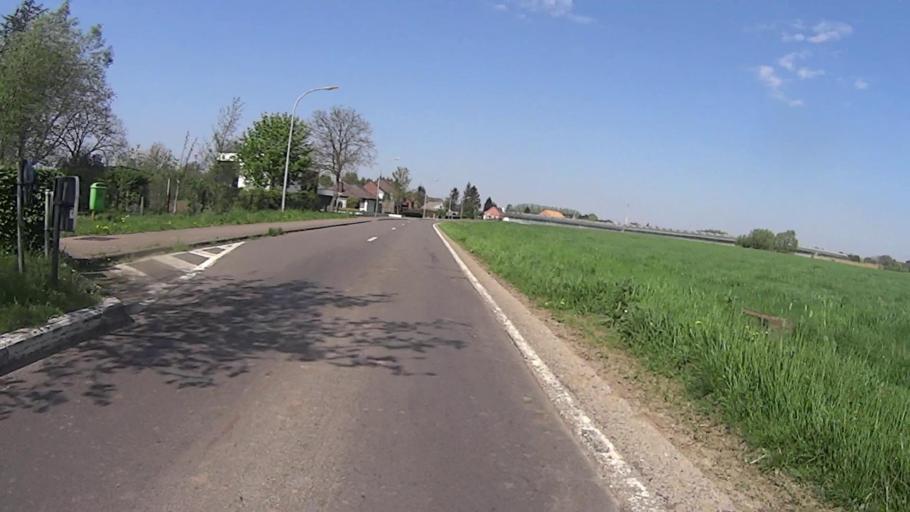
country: BE
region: Flanders
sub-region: Provincie Antwerpen
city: Sint-Amands
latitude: 51.0488
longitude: 4.2321
